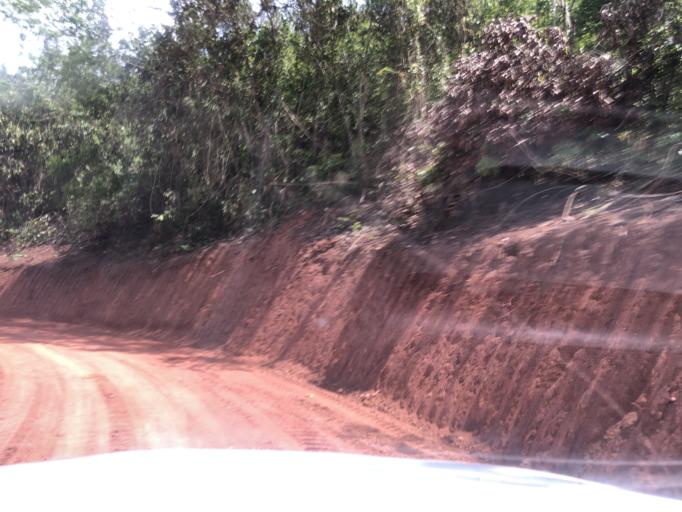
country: CN
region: Yunnan
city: Menglie
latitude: 22.2373
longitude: 101.6171
